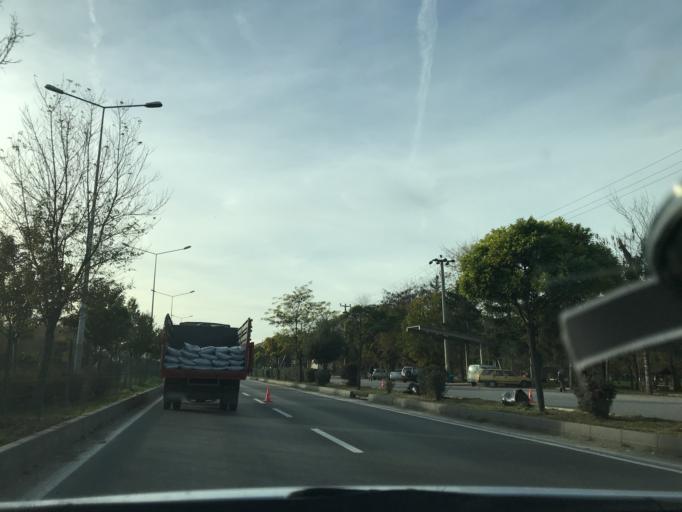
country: TR
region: Bolu
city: Bolu
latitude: 40.7380
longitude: 31.6158
